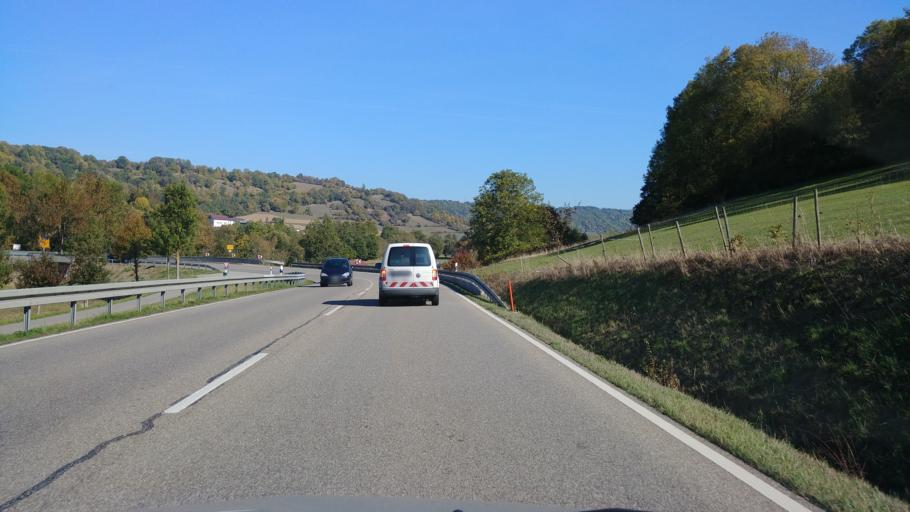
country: DE
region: Baden-Wuerttemberg
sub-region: Regierungsbezirk Stuttgart
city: Untermunkheim
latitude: 49.1492
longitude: 9.7348
